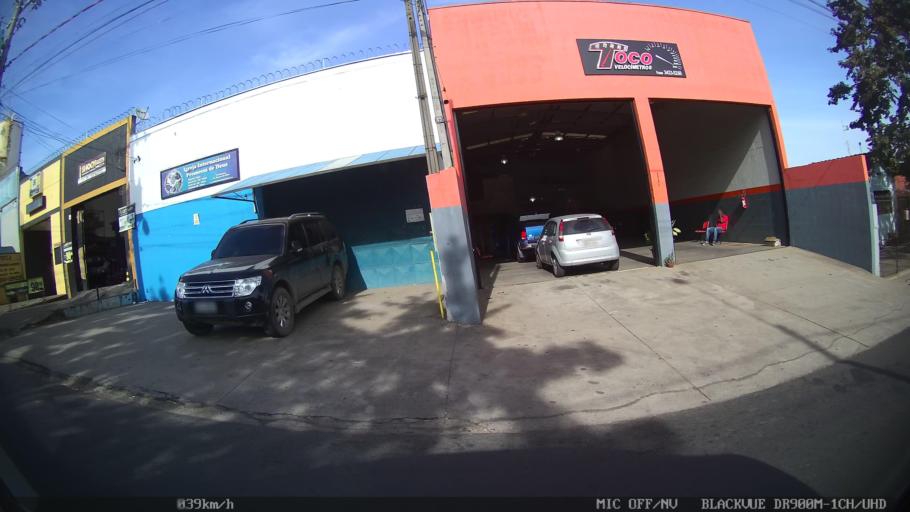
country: BR
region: Sao Paulo
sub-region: Piracicaba
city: Piracicaba
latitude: -22.7531
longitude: -47.6489
